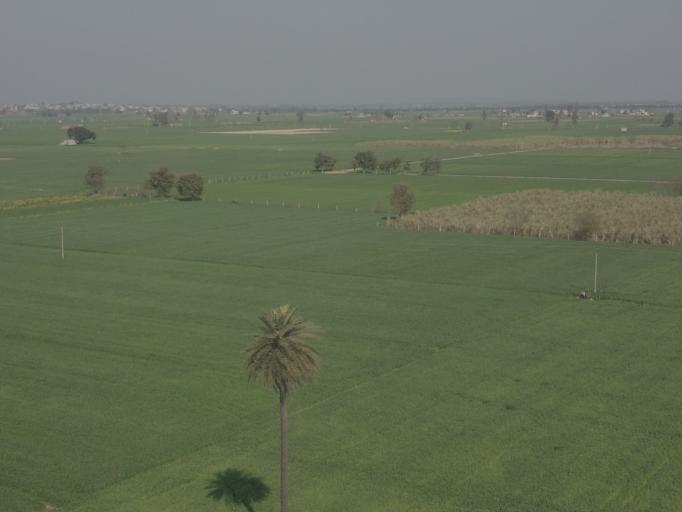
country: IN
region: Punjab
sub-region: Shahid Bhagat Singh Nagar
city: Rahon
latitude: 31.0235
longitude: 76.0892
